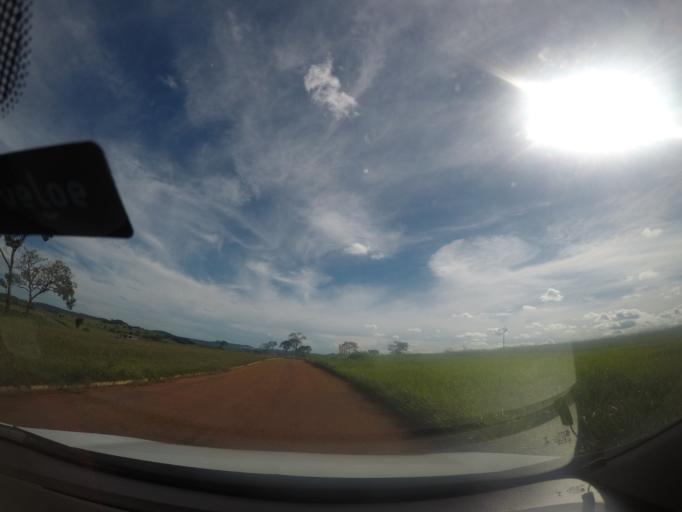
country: BR
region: Goias
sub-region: Inhumas
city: Inhumas
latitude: -16.4077
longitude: -49.4717
